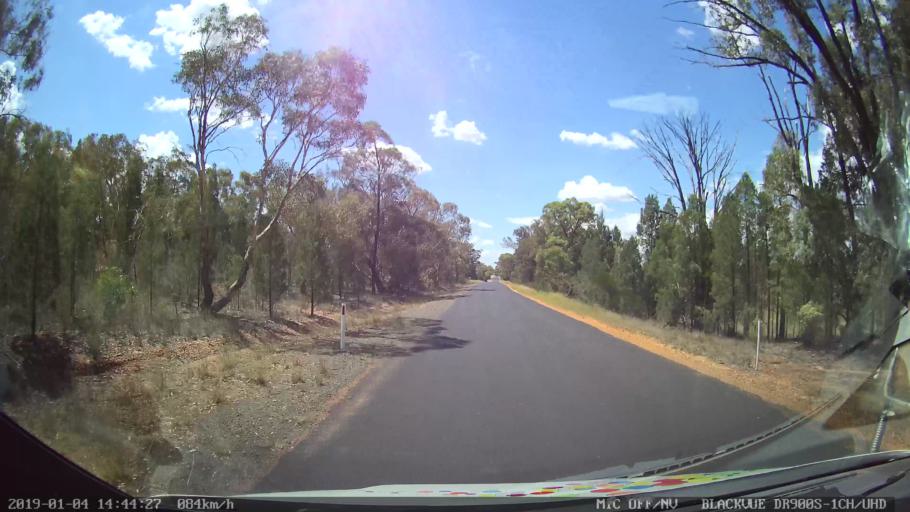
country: AU
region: New South Wales
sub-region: Dubbo Municipality
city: Dubbo
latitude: -32.1060
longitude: 148.6556
